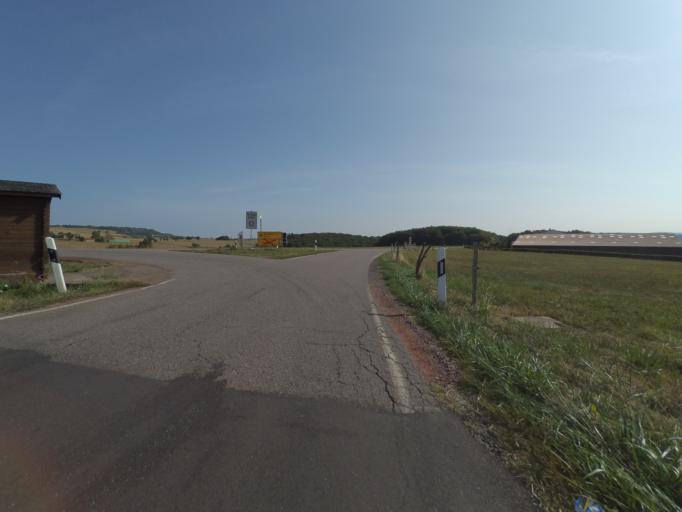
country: DE
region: Rheinland-Pfalz
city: Merzkirchen
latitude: 49.5754
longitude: 6.4949
